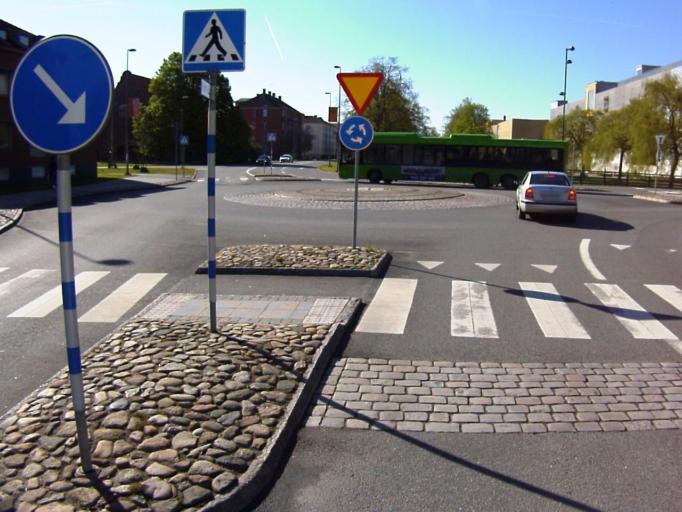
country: SE
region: Skane
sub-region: Kristianstads Kommun
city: Kristianstad
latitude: 56.0325
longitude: 14.1584
